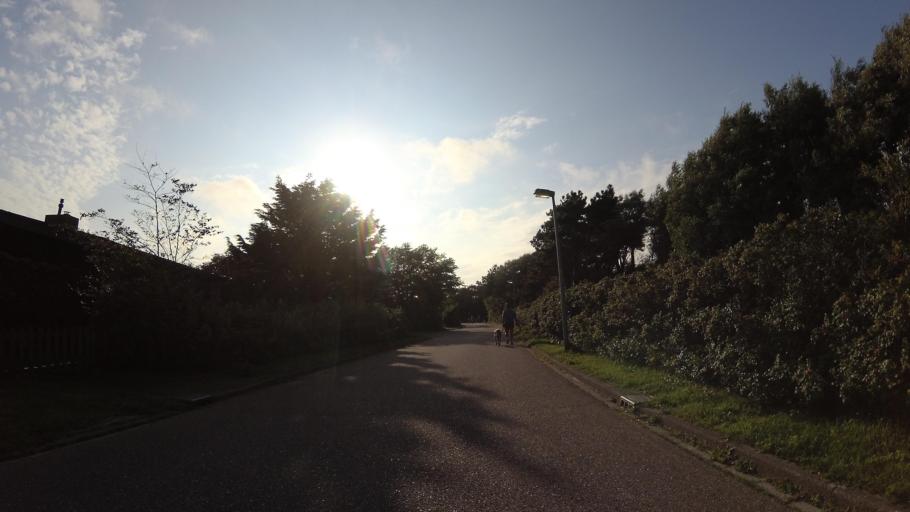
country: NL
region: North Holland
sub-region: Gemeente Den Helder
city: Den Helder
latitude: 52.9053
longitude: 4.7236
